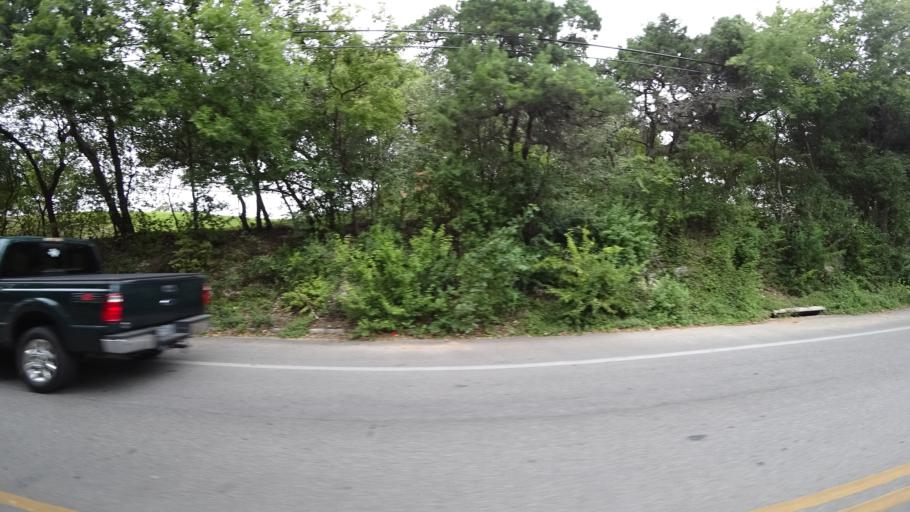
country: US
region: Texas
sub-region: Travis County
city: Austin
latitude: 30.2967
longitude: -97.7257
